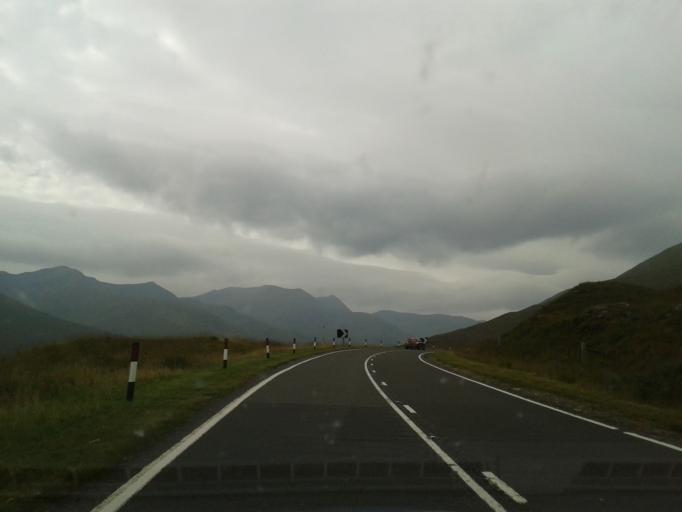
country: GB
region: Scotland
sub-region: Highland
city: Fort William
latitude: 57.1560
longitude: -5.1753
